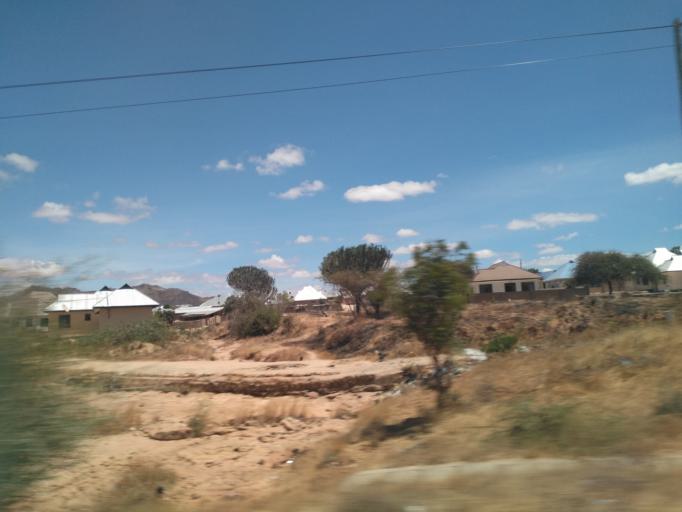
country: TZ
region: Dodoma
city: Kisasa
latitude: -6.1887
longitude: 35.7788
